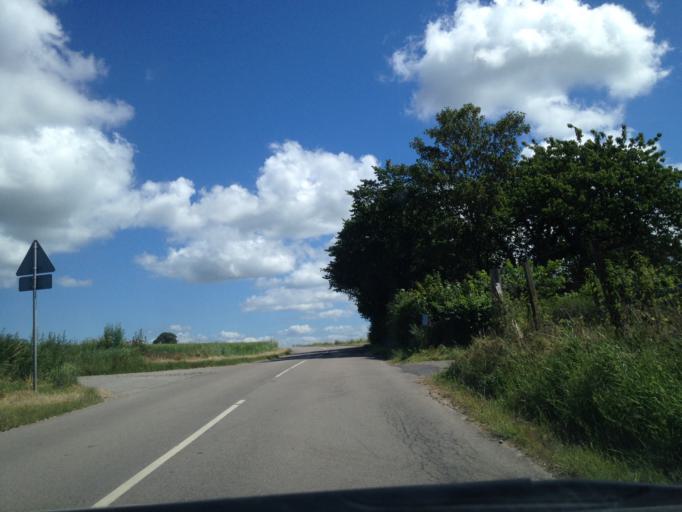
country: DK
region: Zealand
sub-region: Odsherred Kommune
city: Hojby
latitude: 55.9125
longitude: 11.5521
